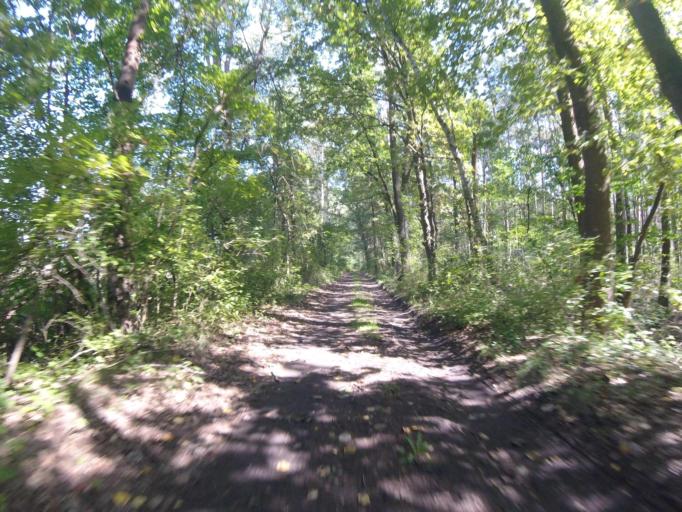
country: DE
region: Brandenburg
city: Bestensee
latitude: 52.2520
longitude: 13.6958
